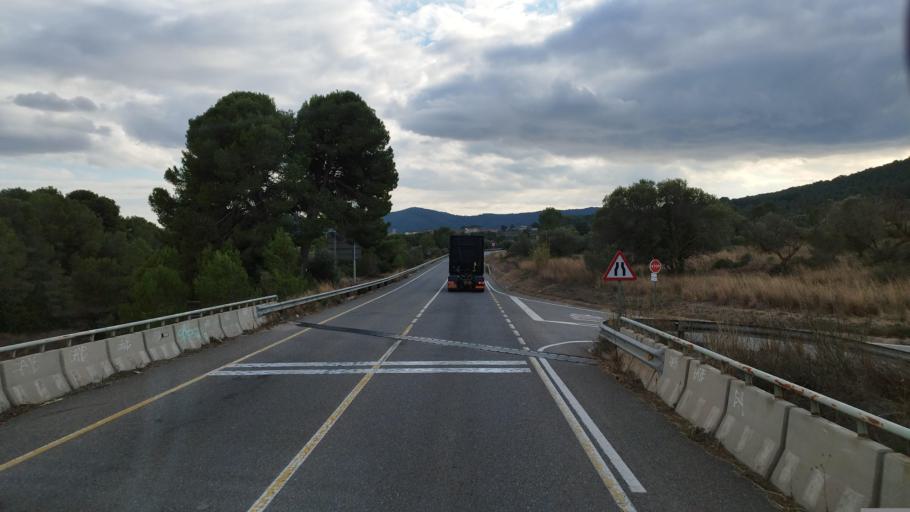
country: ES
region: Catalonia
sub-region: Provincia de Tarragona
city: Albinyana
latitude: 41.2642
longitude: 1.4978
